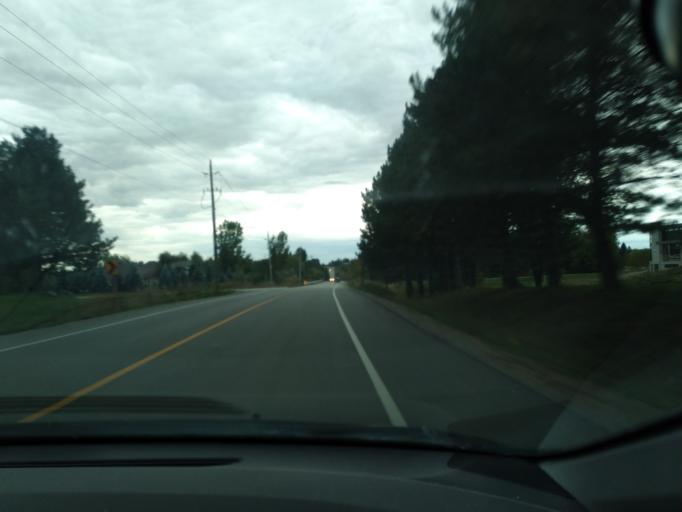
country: CA
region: Ontario
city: Brampton
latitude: 43.9303
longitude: -79.7995
